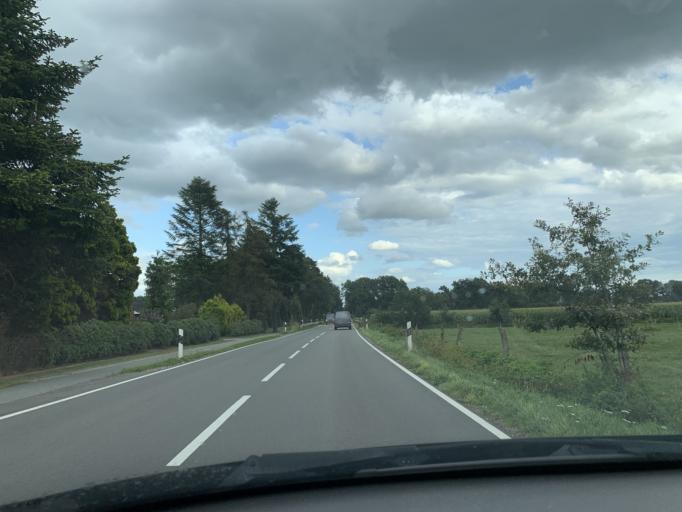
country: DE
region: Lower Saxony
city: Westerstede
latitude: 53.2871
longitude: 8.0161
